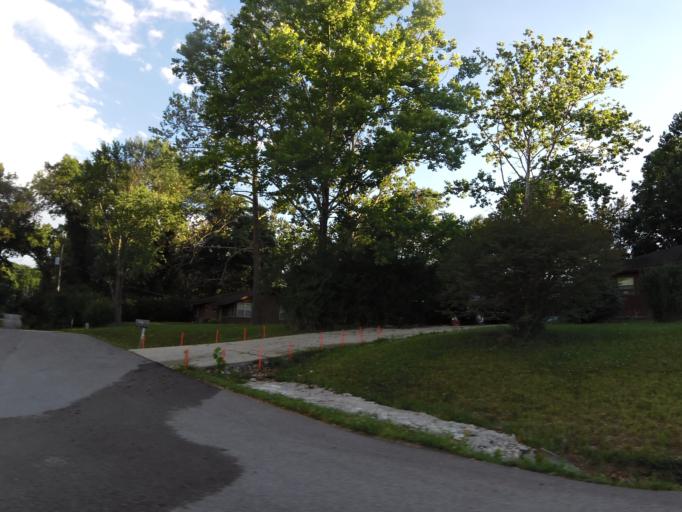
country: US
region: Missouri
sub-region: Jefferson County
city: Byrnes Mill
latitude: 38.4406
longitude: -90.6061
